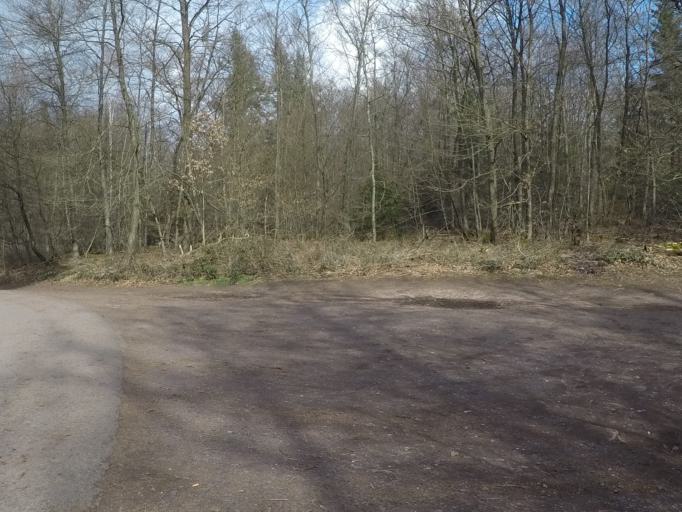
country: DE
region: Rheinland-Pfalz
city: Munchweiler an der Rodalbe
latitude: 49.2133
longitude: 7.7223
